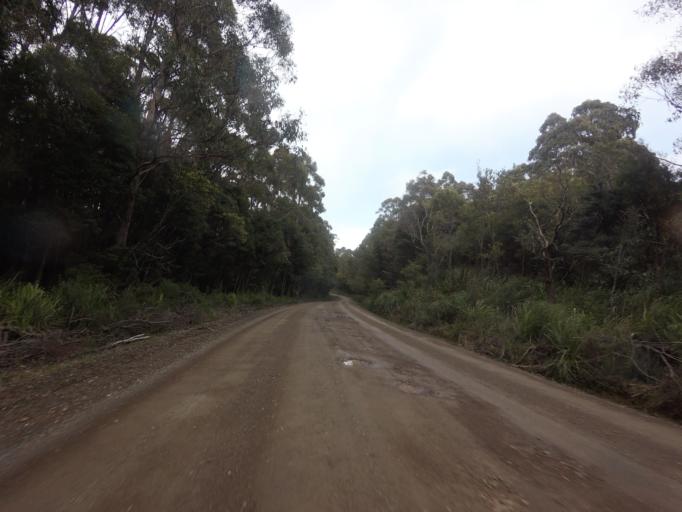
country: AU
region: Tasmania
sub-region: Huon Valley
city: Geeveston
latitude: -43.5202
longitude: 146.8831
